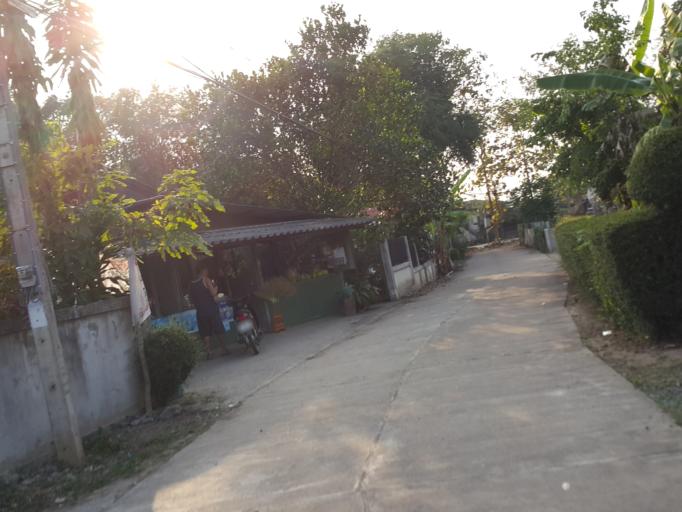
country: TH
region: Chiang Mai
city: San Sai
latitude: 18.8818
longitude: 99.1429
